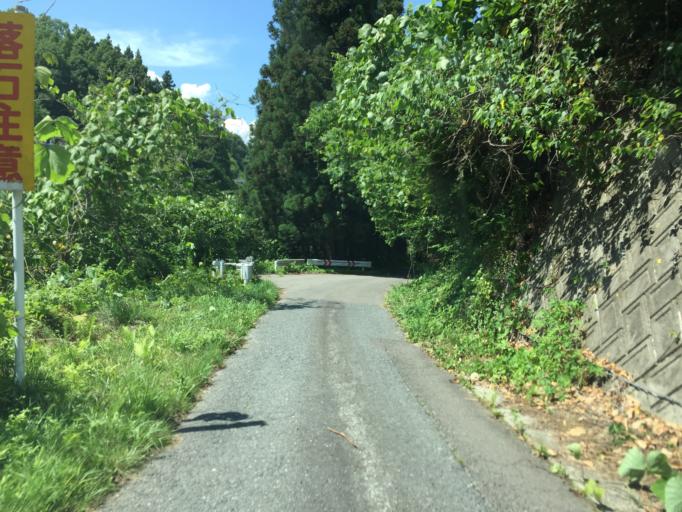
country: JP
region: Fukushima
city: Yanagawamachi-saiwaicho
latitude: 37.7821
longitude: 140.6538
